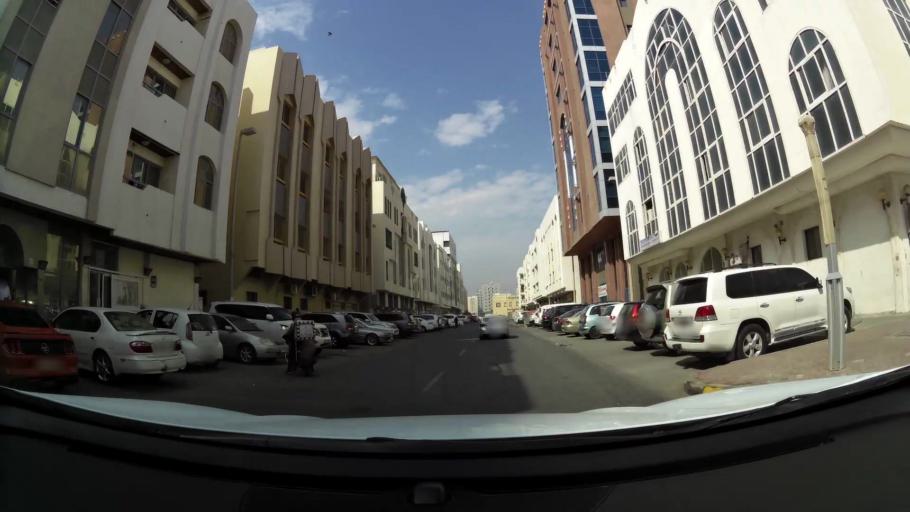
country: AE
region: Abu Dhabi
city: Abu Dhabi
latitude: 24.3363
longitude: 54.5352
